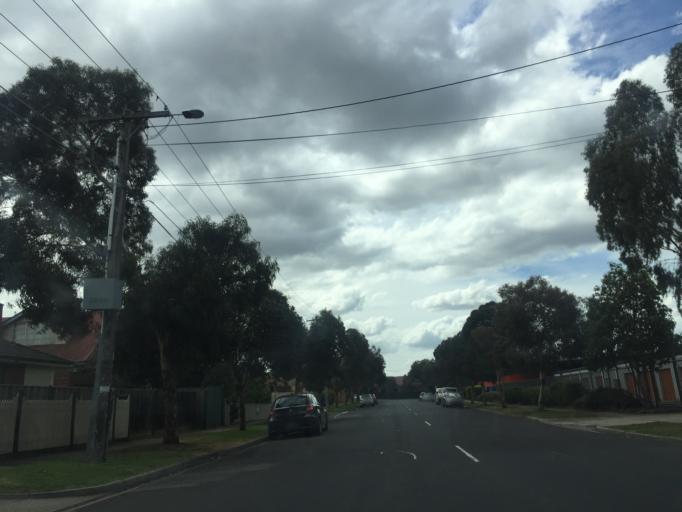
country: AU
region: Victoria
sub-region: Darebin
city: Preston
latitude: -37.7475
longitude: 145.0118
